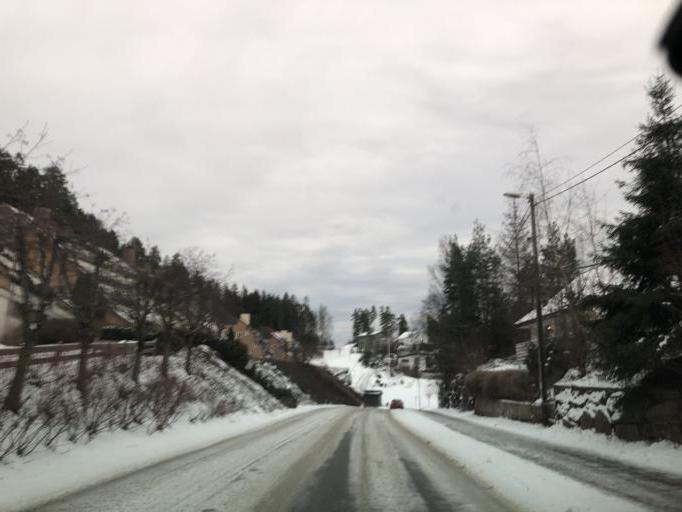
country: NO
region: Akershus
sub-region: Baerum
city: Sandvika
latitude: 59.8673
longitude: 10.5142
